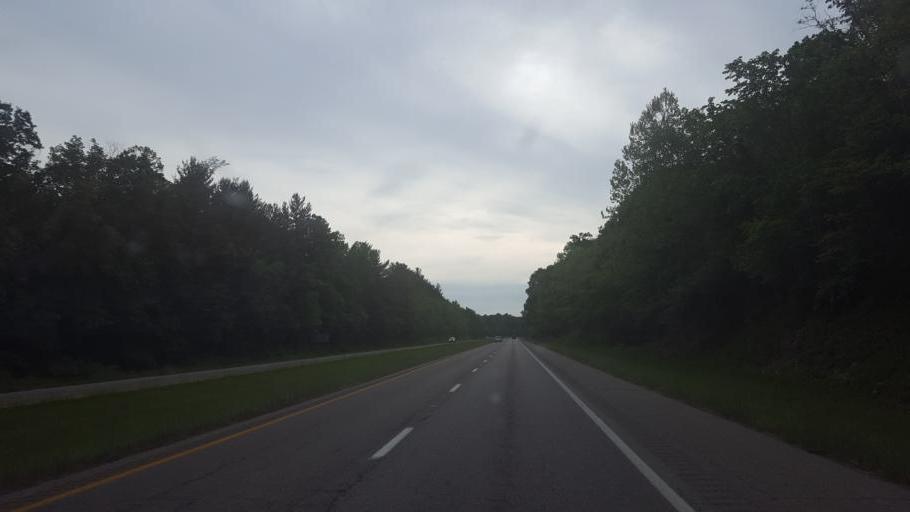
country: US
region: Ohio
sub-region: Jackson County
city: Wellston
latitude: 39.1314
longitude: -82.4106
